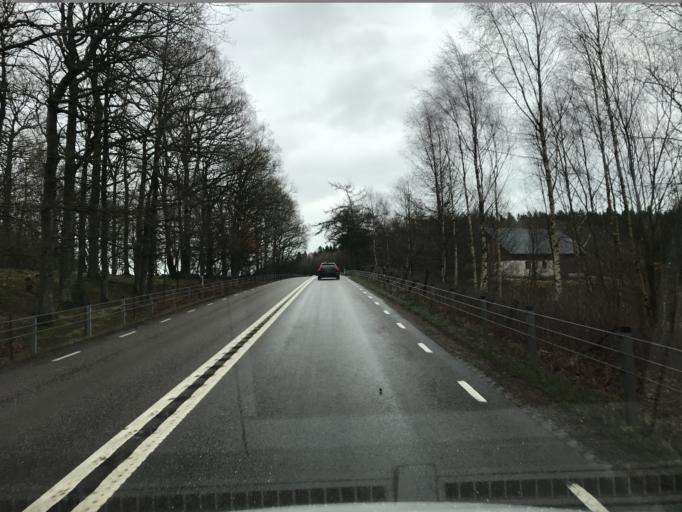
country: SE
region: Skane
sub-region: Klippans Kommun
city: Ljungbyhed
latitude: 56.1017
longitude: 13.1784
